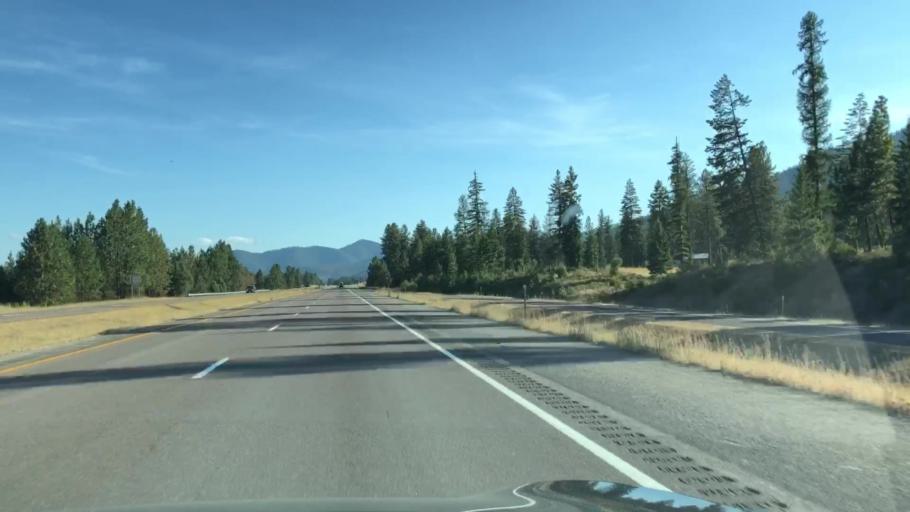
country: US
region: Montana
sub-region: Mineral County
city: Superior
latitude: 47.1061
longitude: -114.7864
